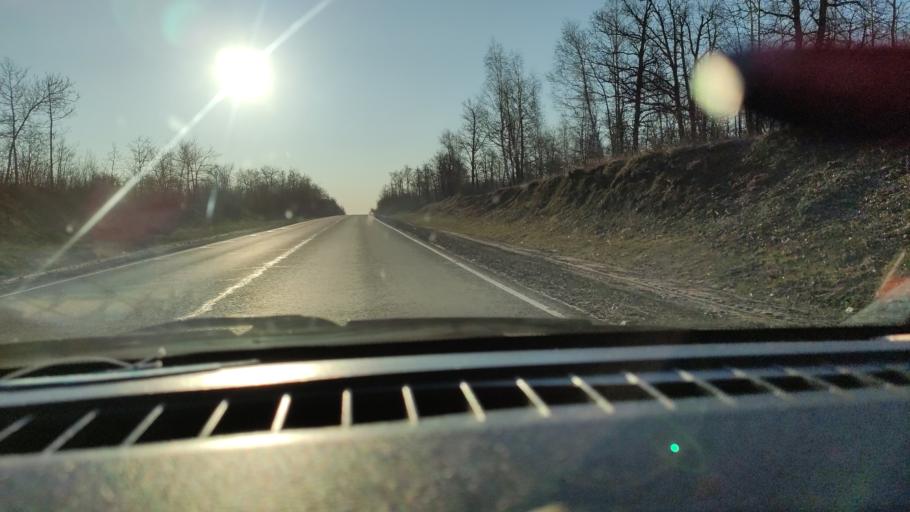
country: RU
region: Saratov
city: Vol'sk
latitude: 52.1103
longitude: 47.3575
